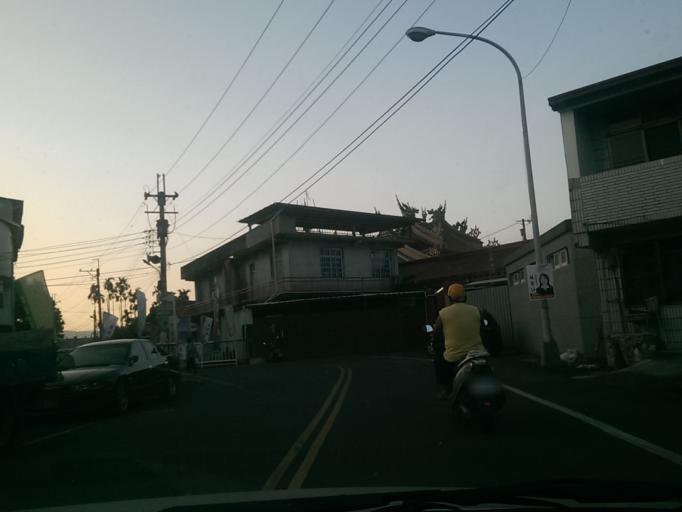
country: TW
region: Taiwan
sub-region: Nantou
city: Puli
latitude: 23.9645
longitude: 120.9621
